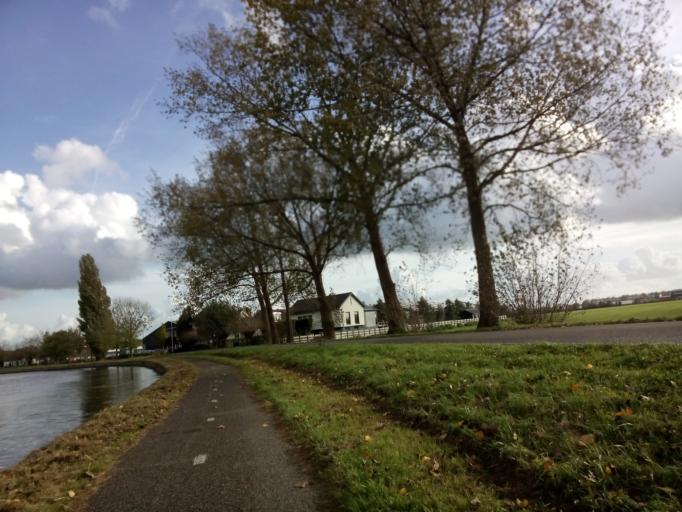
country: NL
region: Utrecht
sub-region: Gemeente Woerden
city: Woerden
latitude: 52.0785
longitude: 4.8278
